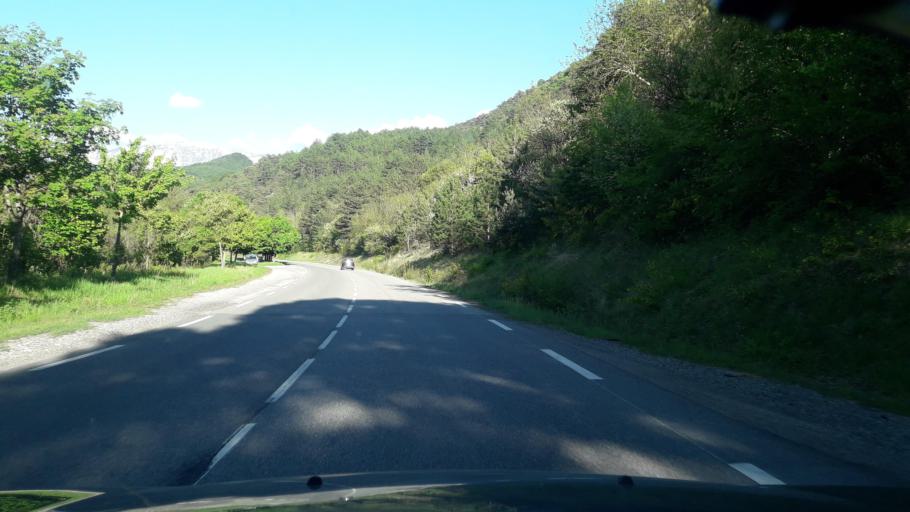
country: FR
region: Rhone-Alpes
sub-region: Departement de la Drome
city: Die
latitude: 44.7628
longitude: 5.3017
